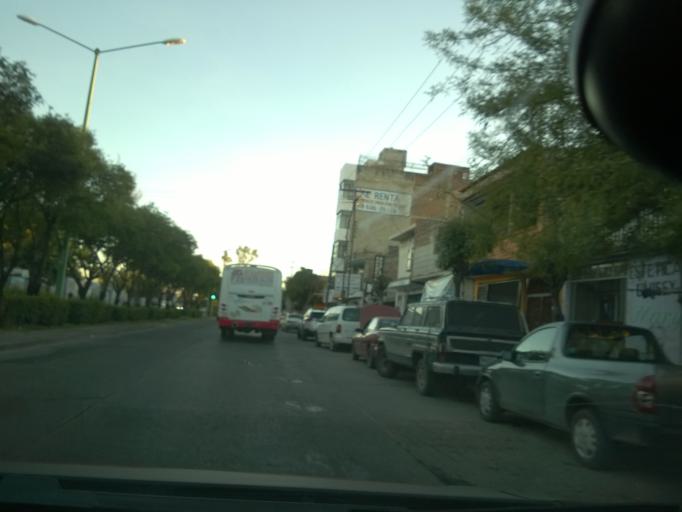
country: MX
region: Guanajuato
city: Leon
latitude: 21.1027
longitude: -101.6791
